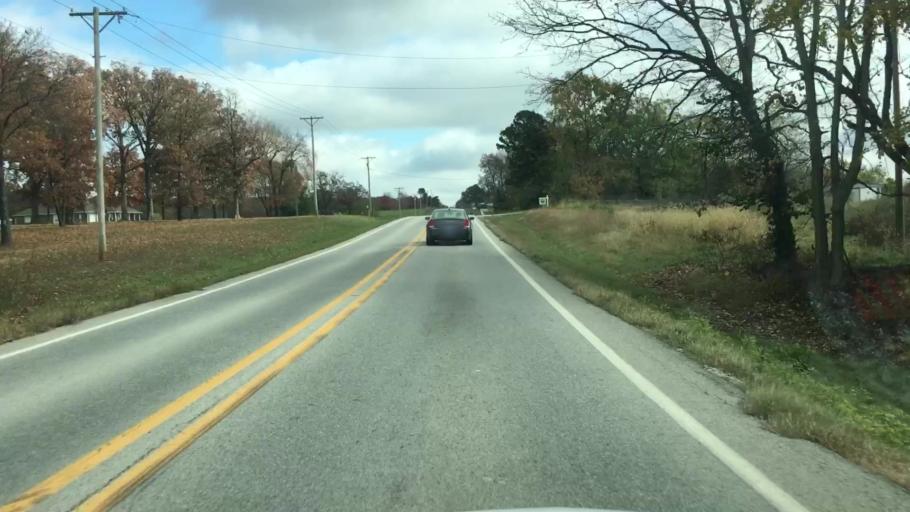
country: US
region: Arkansas
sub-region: Benton County
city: Gentry
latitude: 36.2634
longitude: -94.4607
